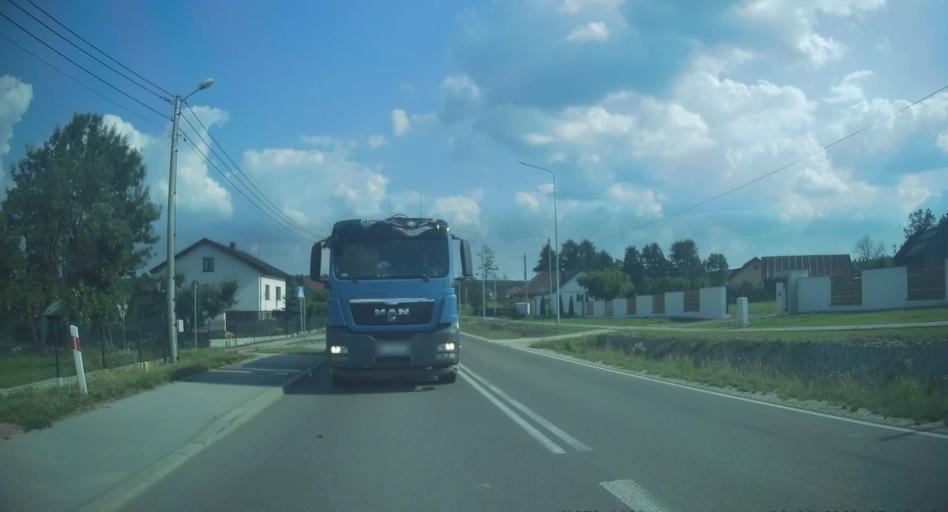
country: PL
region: Swietokrzyskie
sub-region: Powiat konecki
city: Radoszyce
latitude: 51.0322
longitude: 20.2882
